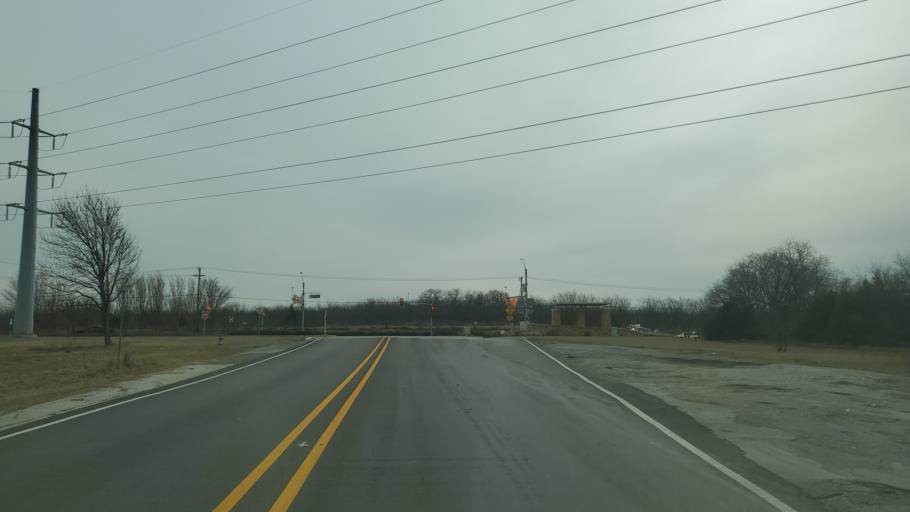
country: US
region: Texas
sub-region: Tarrant County
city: Grapevine
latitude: 32.9498
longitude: -97.0559
